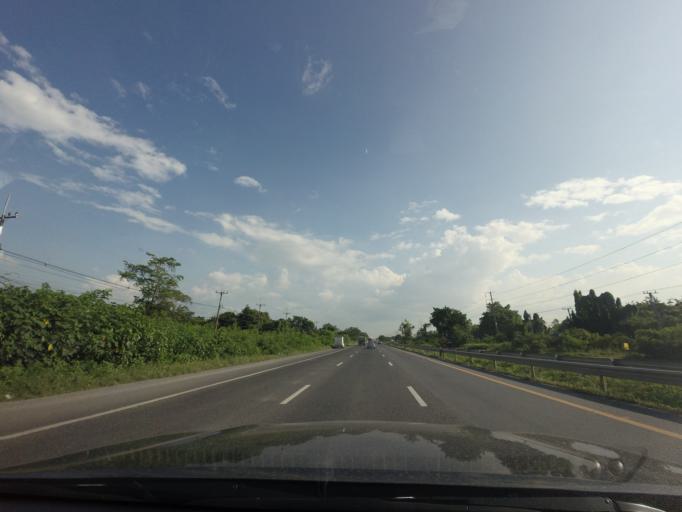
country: TH
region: Sara Buri
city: Chaloem Phra Kiat
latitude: 14.6262
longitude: 100.8902
